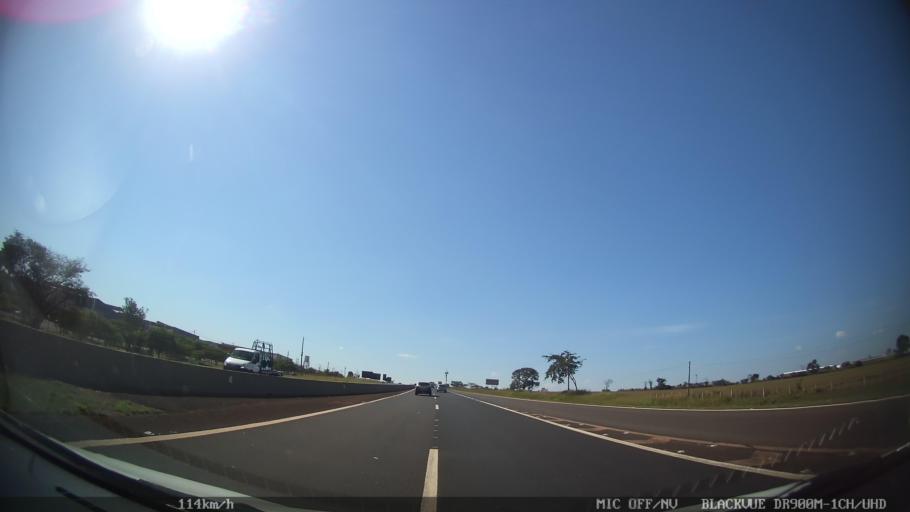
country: BR
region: Sao Paulo
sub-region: Ribeirao Preto
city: Ribeirao Preto
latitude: -21.0990
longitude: -47.7984
